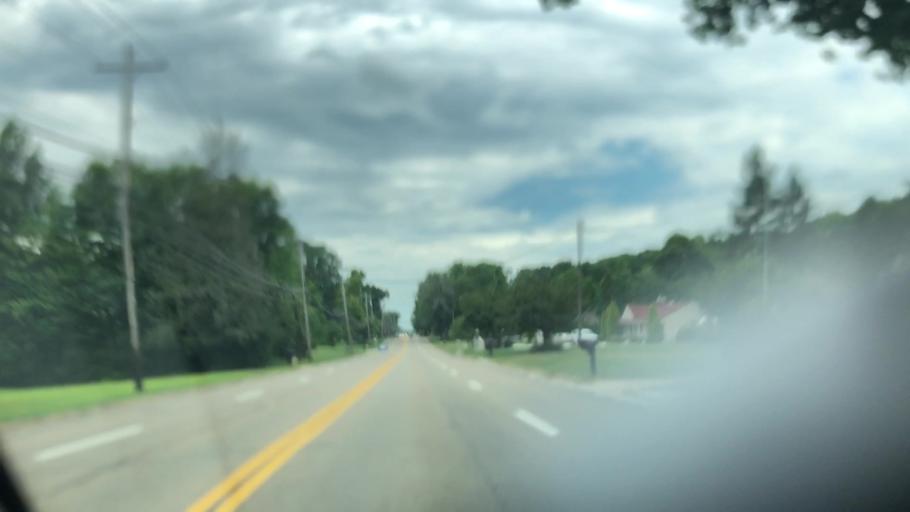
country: US
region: Ohio
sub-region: Summit County
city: Fairlawn
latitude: 41.1179
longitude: -81.6098
